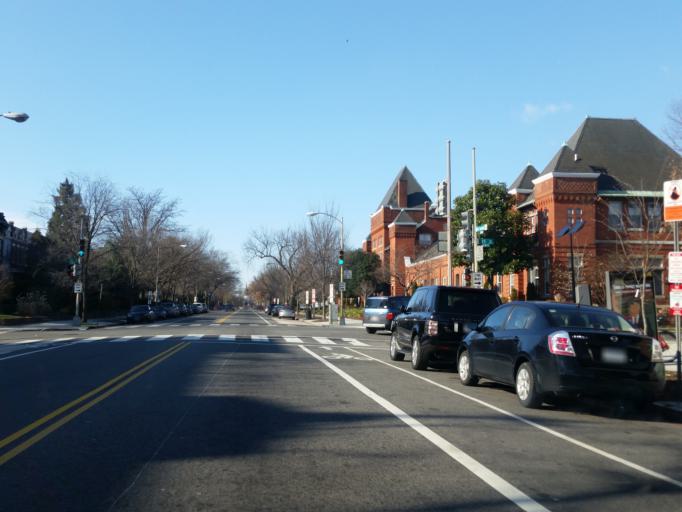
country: US
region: Washington, D.C.
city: Washington, D.C.
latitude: 38.8898
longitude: -76.9832
